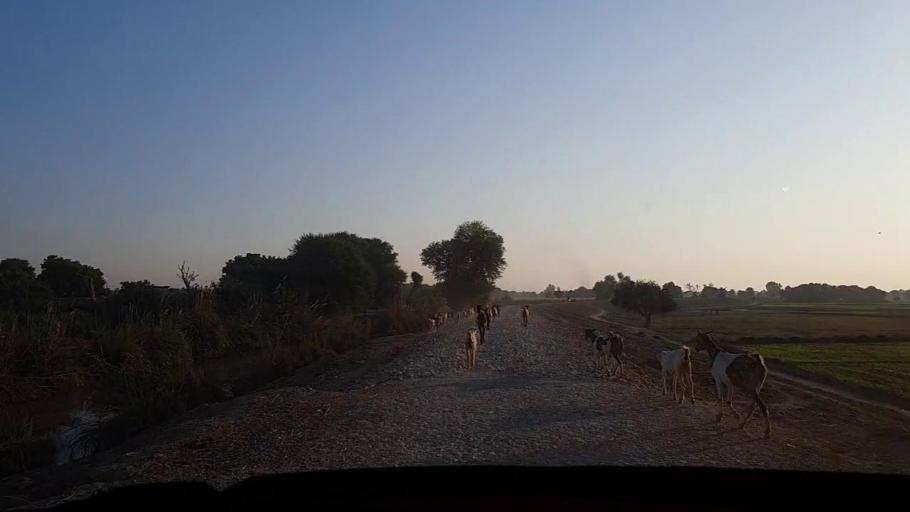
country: PK
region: Sindh
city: Sobhadero
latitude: 27.3698
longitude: 68.3776
